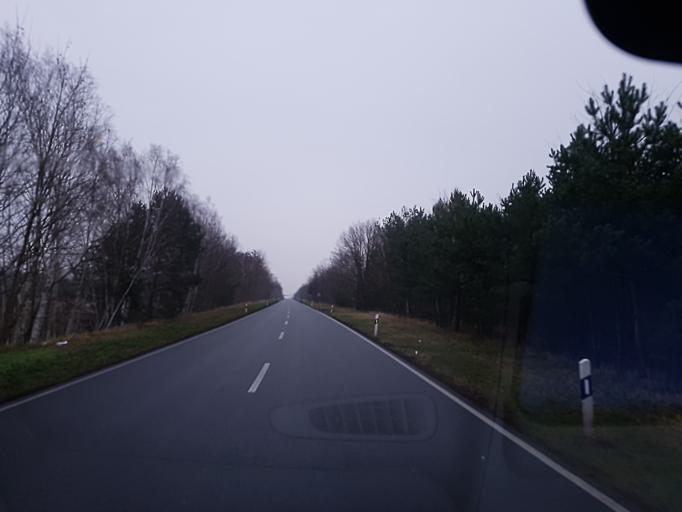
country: DE
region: Brandenburg
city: Lubbenau
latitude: 51.8367
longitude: 13.9360
